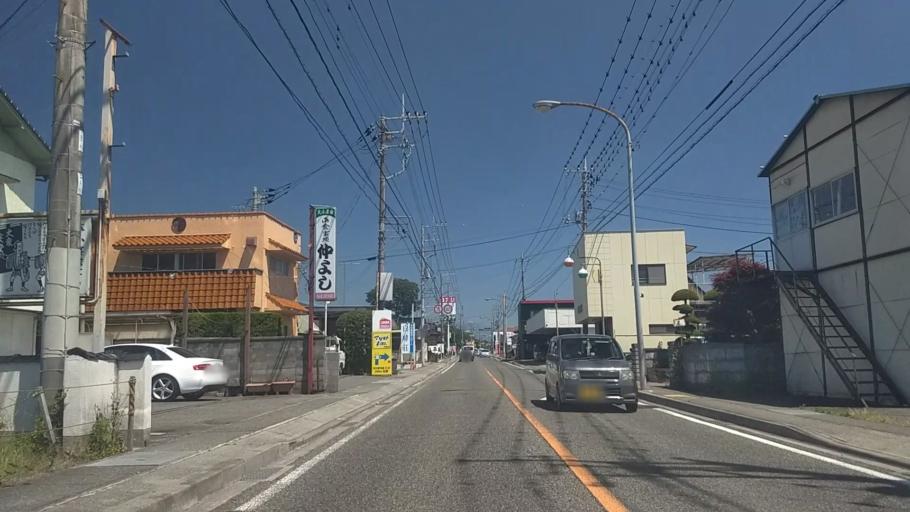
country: JP
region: Yamanashi
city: Ryuo
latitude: 35.6410
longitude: 138.4645
